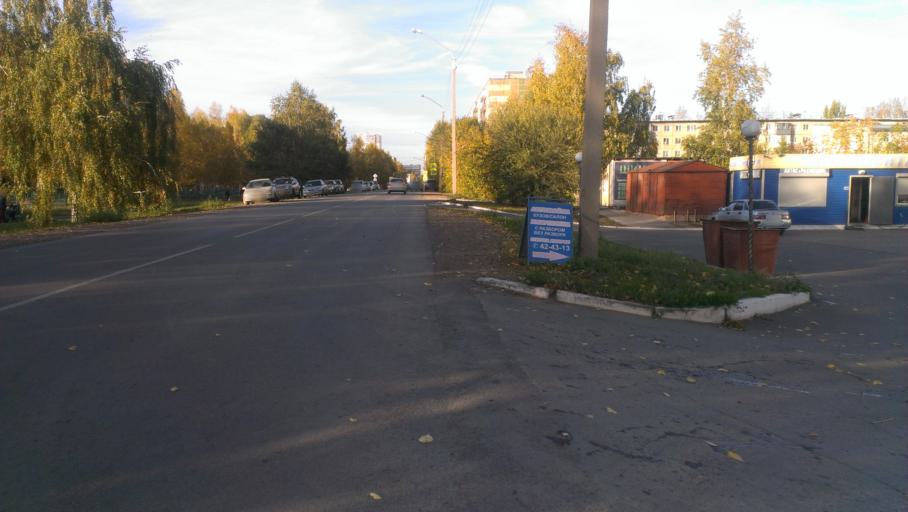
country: RU
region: Altai Krai
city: Novosilikatnyy
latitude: 53.3501
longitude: 83.6765
